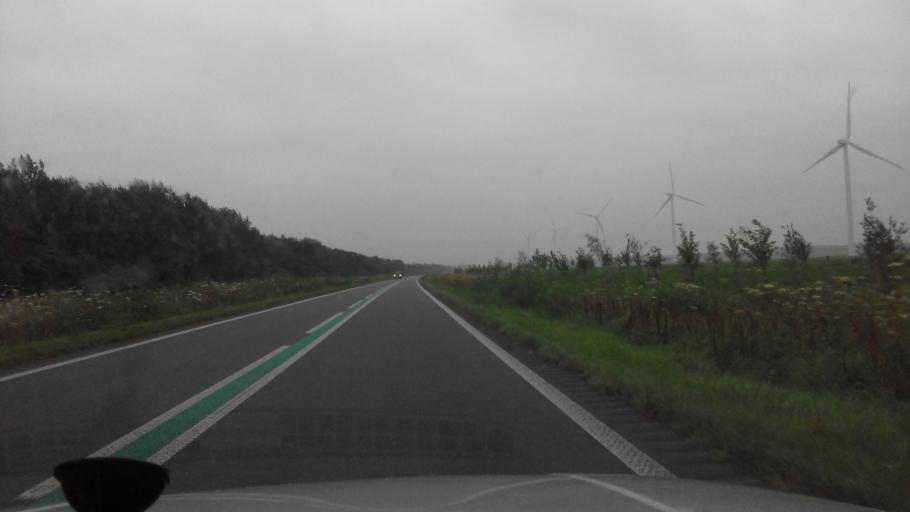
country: NL
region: Gelderland
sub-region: Gemeente Nijkerk
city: Nijkerk
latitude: 52.3035
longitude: 5.4504
